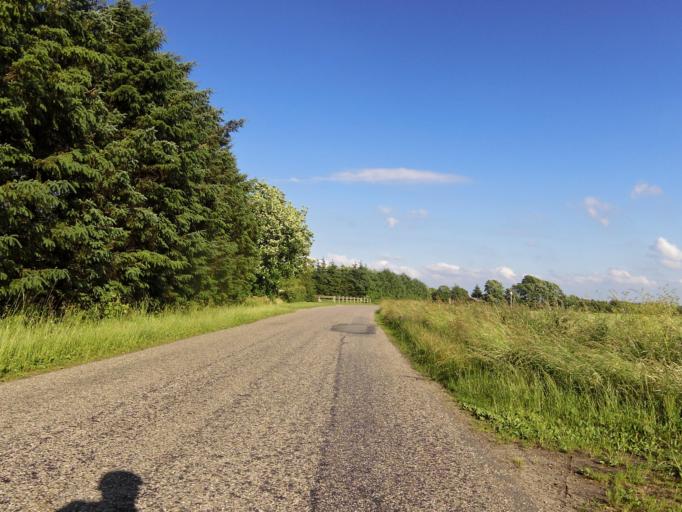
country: DK
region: South Denmark
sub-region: Vejen Kommune
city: Rodding
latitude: 55.3454
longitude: 9.1364
